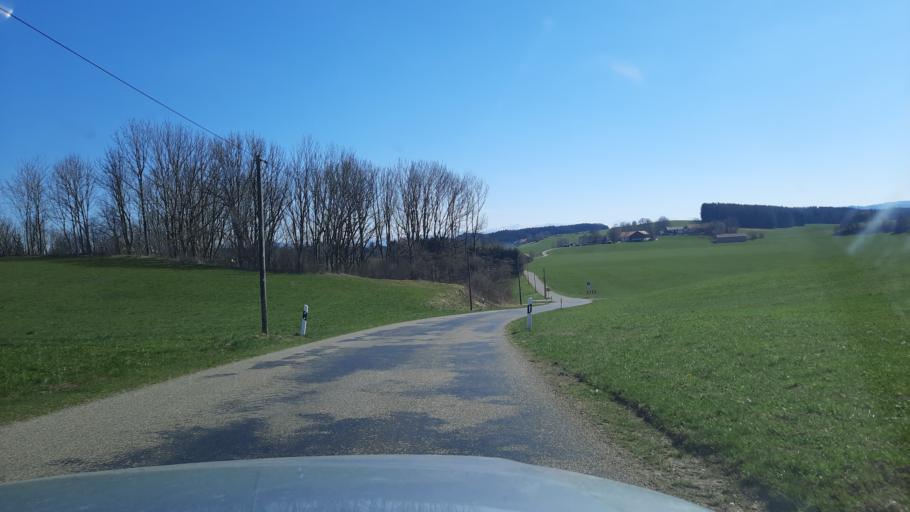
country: DE
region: Bavaria
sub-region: Swabia
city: Wolfertschwenden
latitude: 47.8564
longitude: 10.2475
